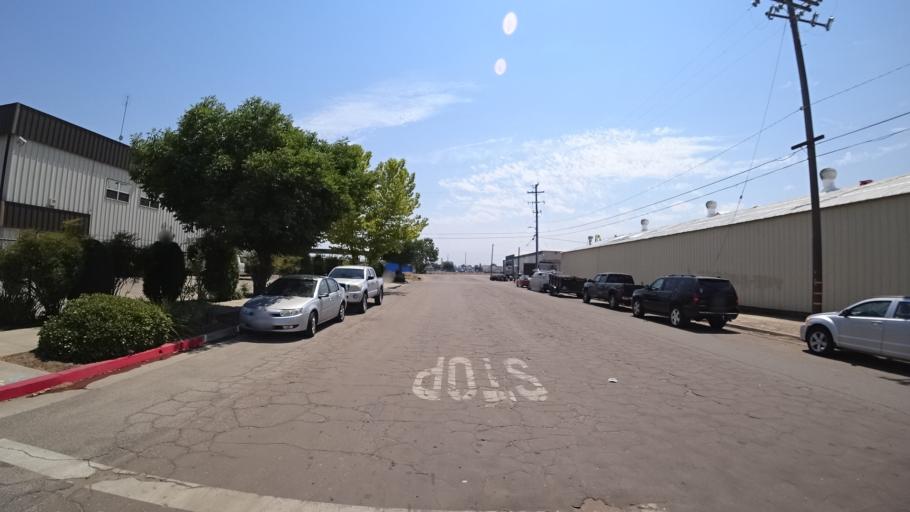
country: US
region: California
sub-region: Fresno County
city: Fresno
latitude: 36.7227
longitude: -119.7762
